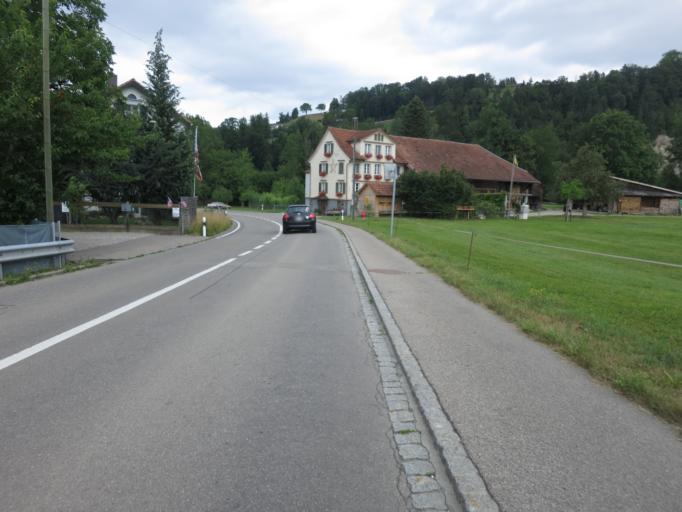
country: CH
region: Saint Gallen
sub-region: Wahlkreis Toggenburg
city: Lutisburg
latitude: 47.3907
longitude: 9.0864
